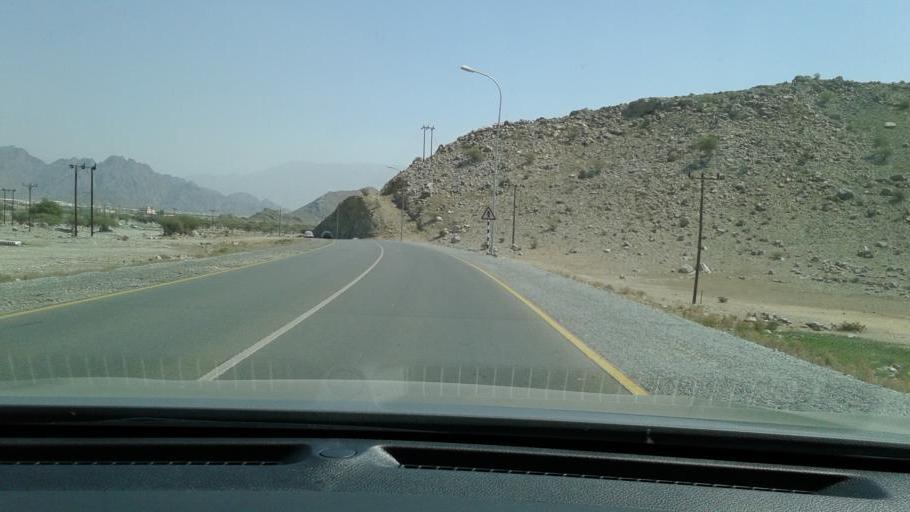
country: OM
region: Al Batinah
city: Rustaq
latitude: 23.3701
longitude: 57.4560
